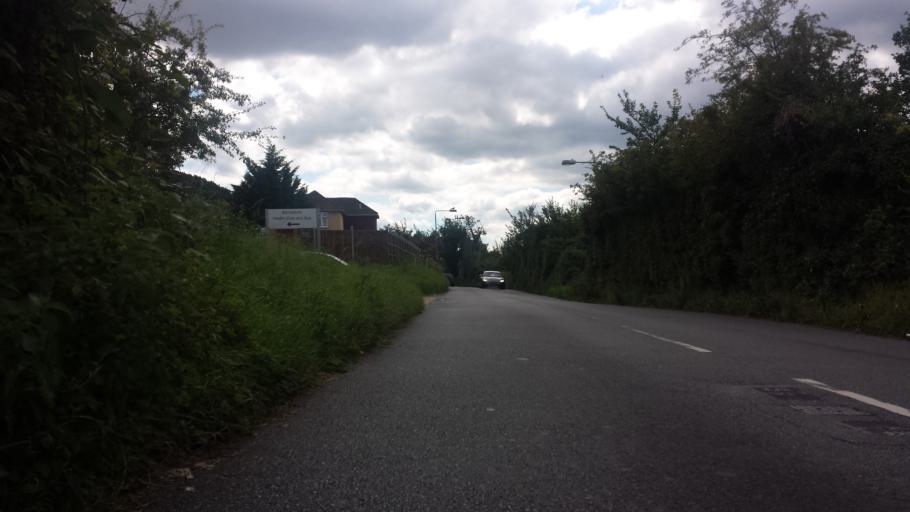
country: GB
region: England
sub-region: Greater London
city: Sidcup
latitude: 51.4097
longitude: 0.1246
